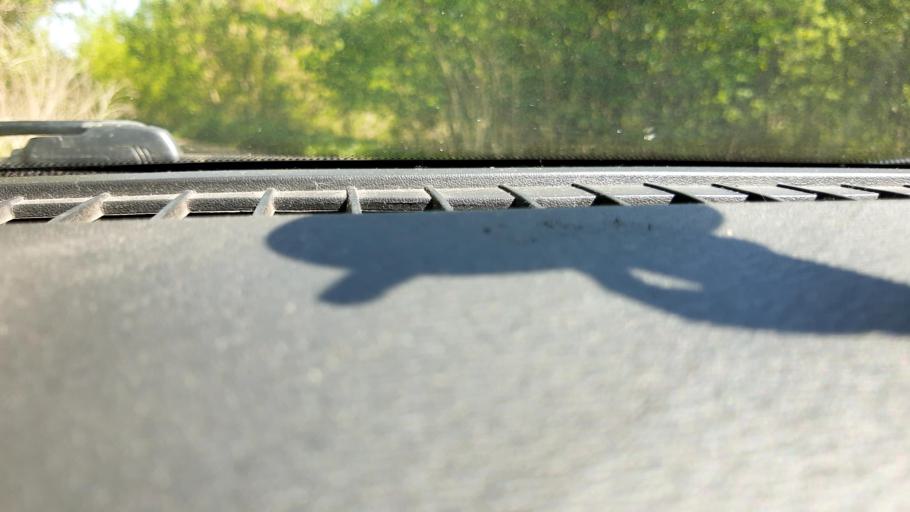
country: RU
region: Bashkortostan
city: Iglino
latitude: 54.7718
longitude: 56.1943
